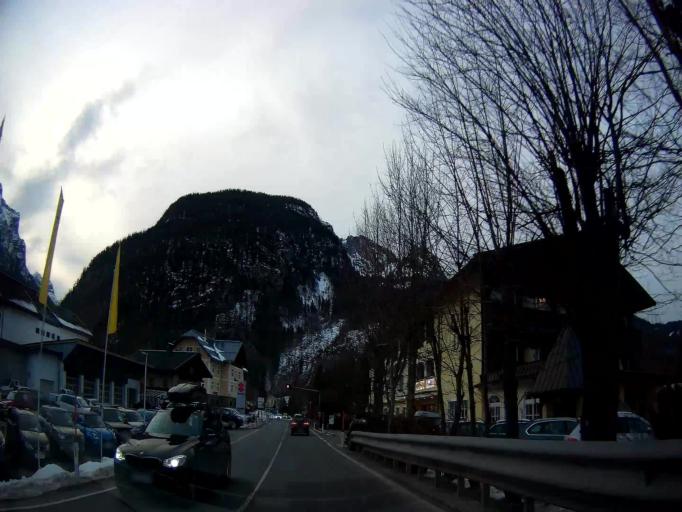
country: AT
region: Salzburg
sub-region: Politischer Bezirk Zell am See
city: Lofer
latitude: 47.5878
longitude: 12.6984
